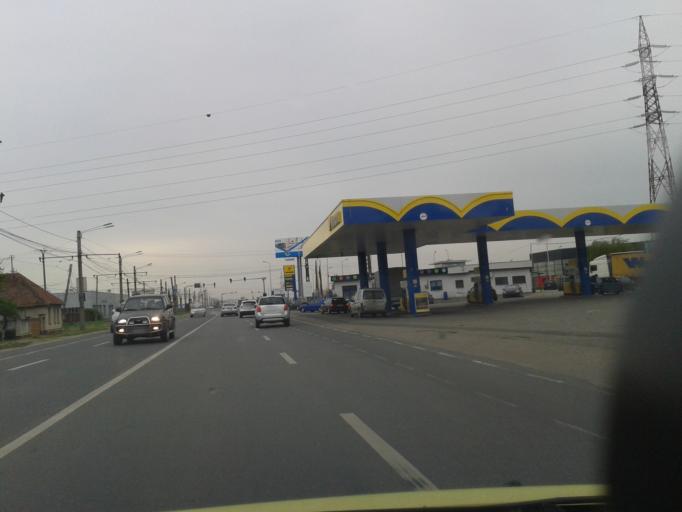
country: RO
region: Arad
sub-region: Comuna Vladimirescu
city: Vladimirescu
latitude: 46.1752
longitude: 21.3665
